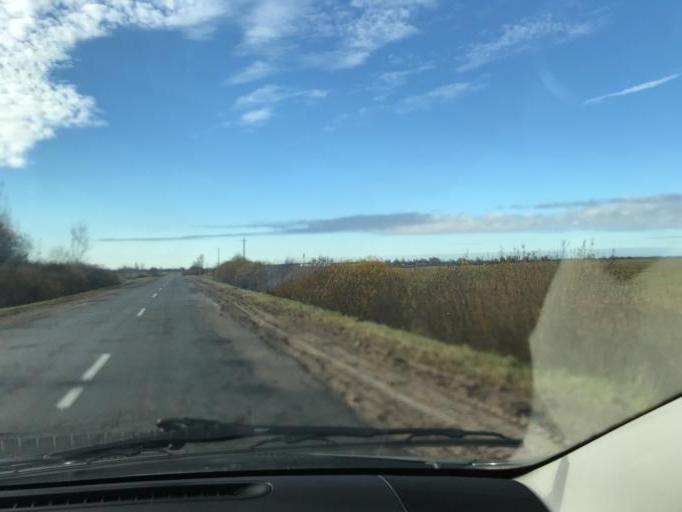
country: BY
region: Vitebsk
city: Haradok
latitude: 55.3812
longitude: 29.6483
